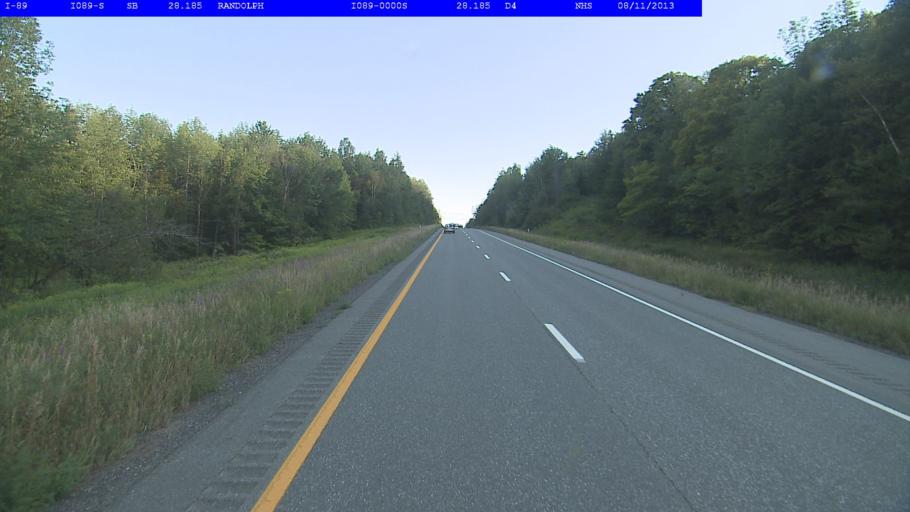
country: US
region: Vermont
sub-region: Orange County
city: Randolph
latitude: 43.9066
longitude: -72.6143
